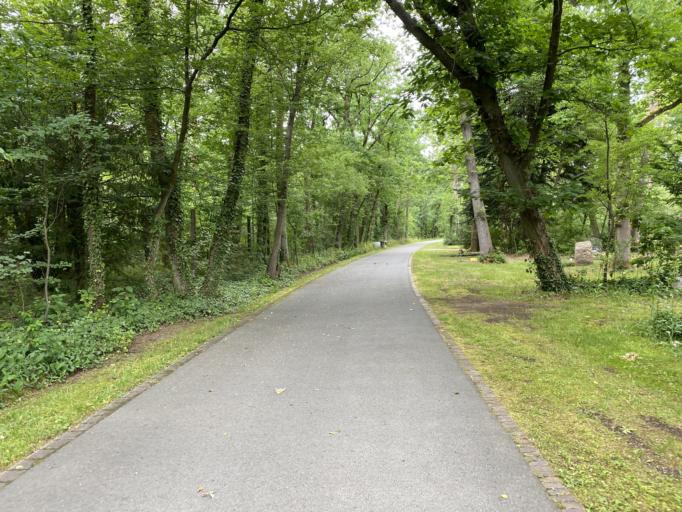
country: DE
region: Hesse
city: Griesheim
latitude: 49.8717
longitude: 8.6084
